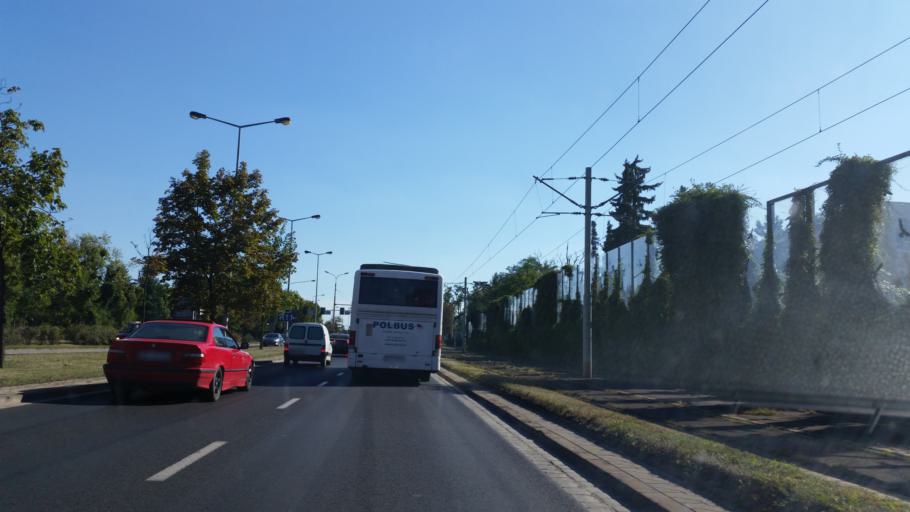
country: PL
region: Lower Silesian Voivodeship
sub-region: Powiat wroclawski
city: Wroclaw
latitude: 51.0706
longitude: 17.0054
